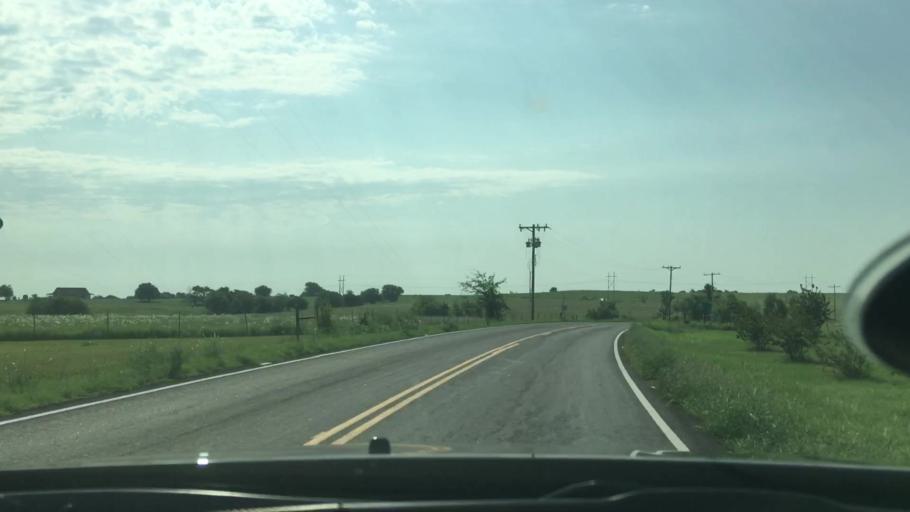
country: US
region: Oklahoma
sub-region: Bryan County
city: Durant
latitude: 34.1426
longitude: -96.4980
